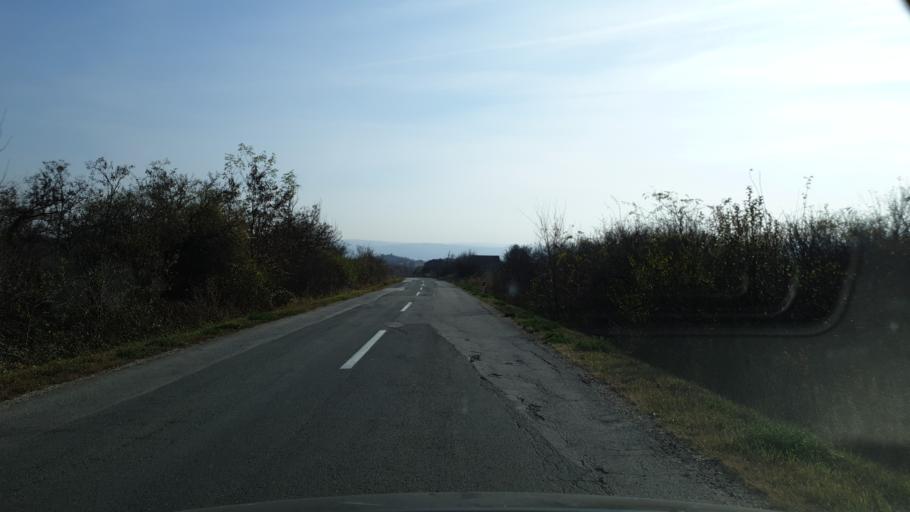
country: RS
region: Central Serbia
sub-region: Borski Okrug
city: Bor
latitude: 43.9794
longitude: 22.0732
